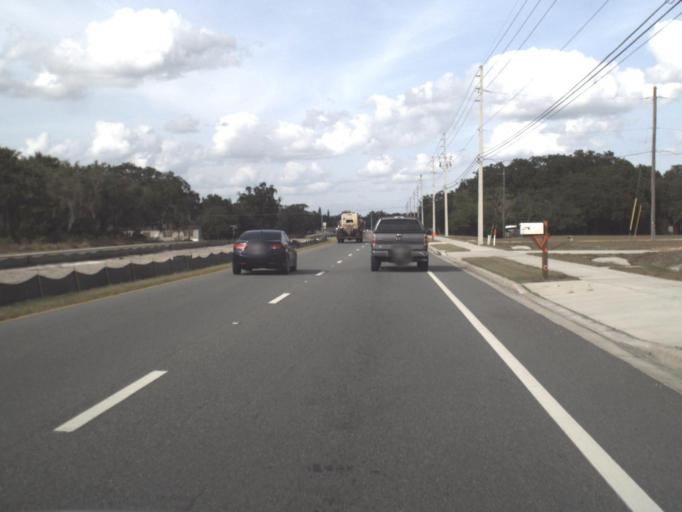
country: US
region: Florida
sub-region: Osceola County
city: Saint Cloud
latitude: 28.2852
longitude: -81.2439
